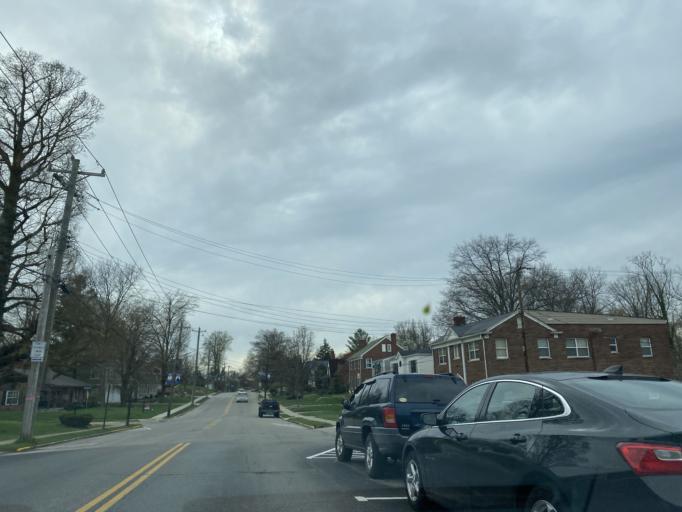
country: US
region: Kentucky
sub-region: Campbell County
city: Fort Thomas
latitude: 39.0764
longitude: -84.4539
